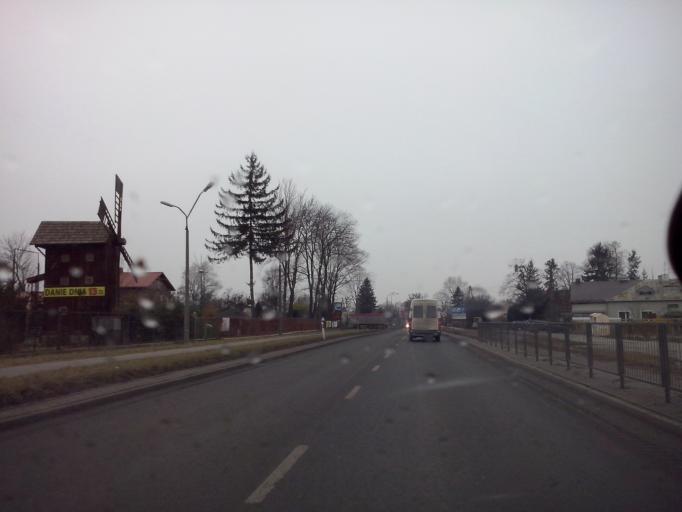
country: PL
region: Lublin Voivodeship
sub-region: Powiat zamojski
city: Michalow
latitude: 50.7140
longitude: 23.0130
